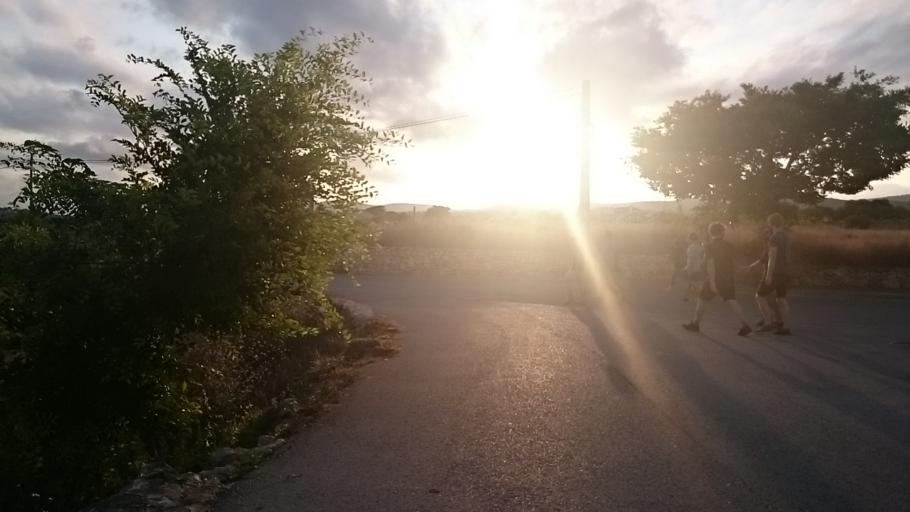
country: ES
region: Catalonia
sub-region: Provincia de Barcelona
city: Vilanova i la Geltru
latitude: 41.2426
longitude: 1.7193
